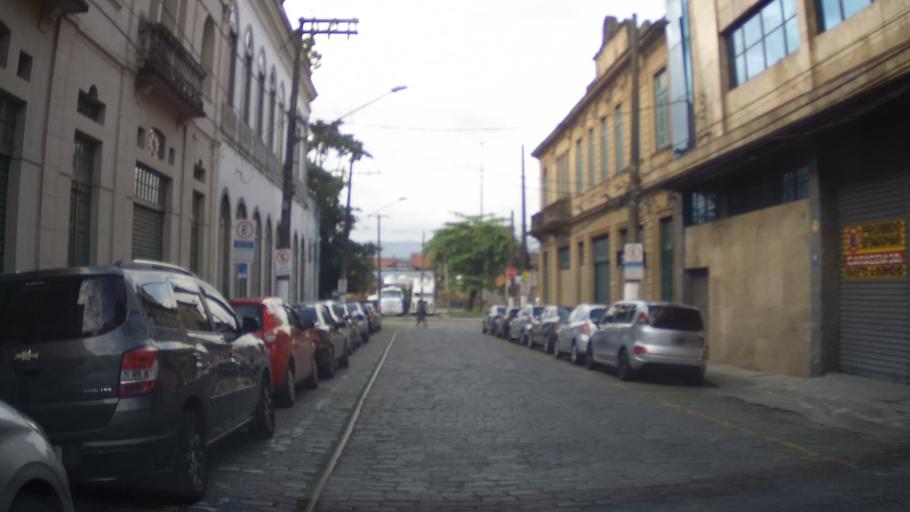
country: BR
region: Sao Paulo
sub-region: Santos
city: Santos
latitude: -23.9320
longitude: -46.3318
